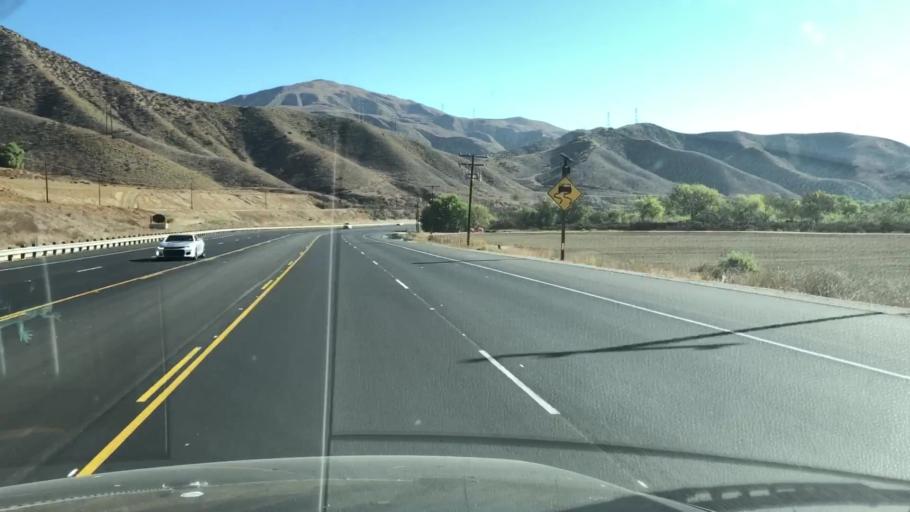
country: US
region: California
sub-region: Ventura County
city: Piru
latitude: 34.4088
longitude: -118.7343
